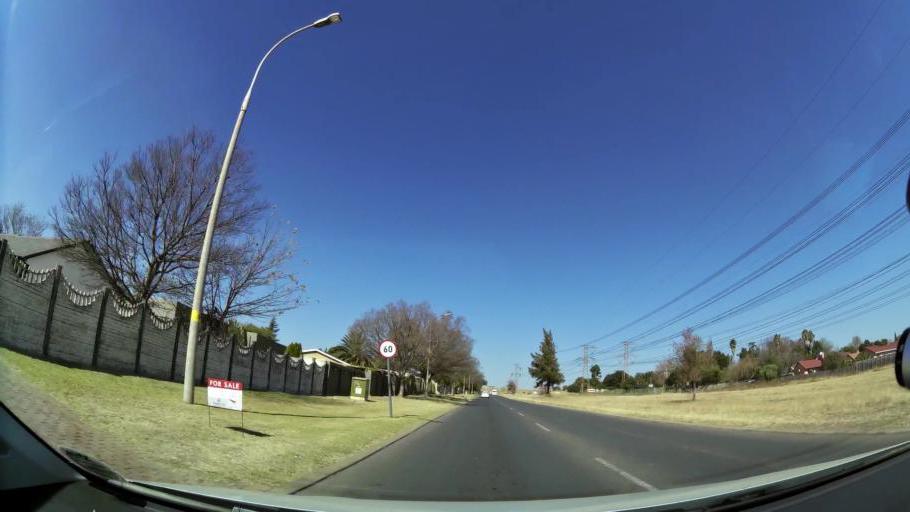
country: ZA
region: Gauteng
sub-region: City of Johannesburg Metropolitan Municipality
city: Modderfontein
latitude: -26.0585
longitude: 28.2146
